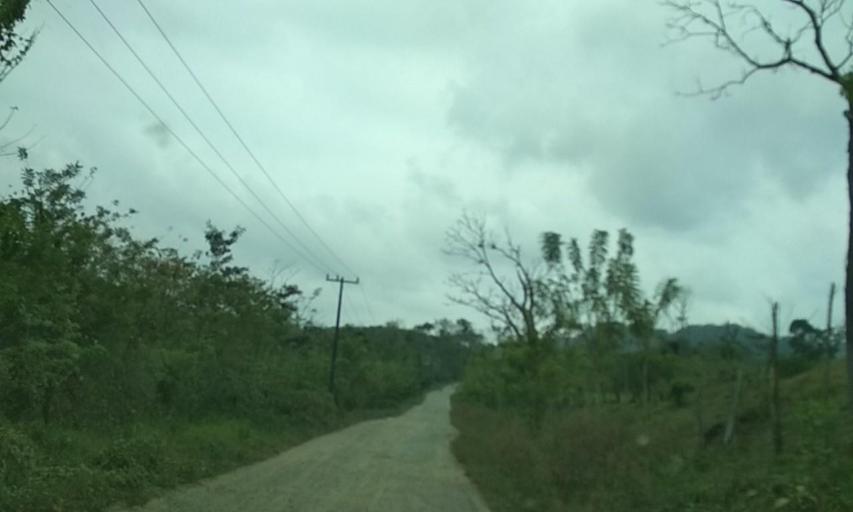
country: MX
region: Veracruz
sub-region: Uxpanapa
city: Poblado 10
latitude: 17.4830
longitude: -94.1269
